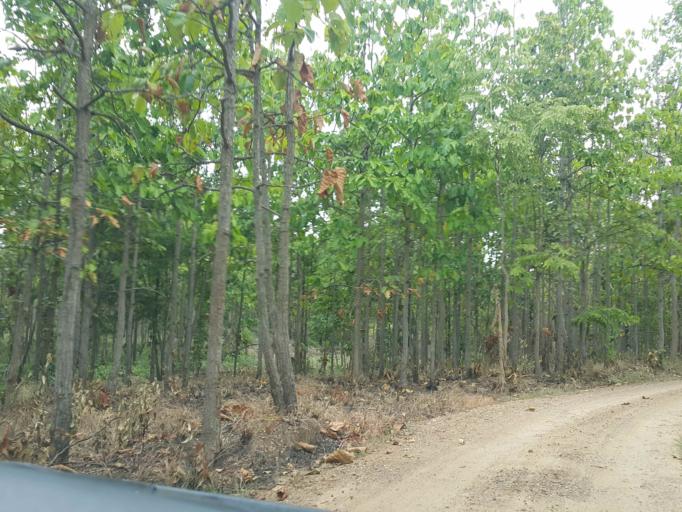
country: TH
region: Chiang Mai
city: Doi Lo
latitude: 18.5064
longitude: 98.7415
